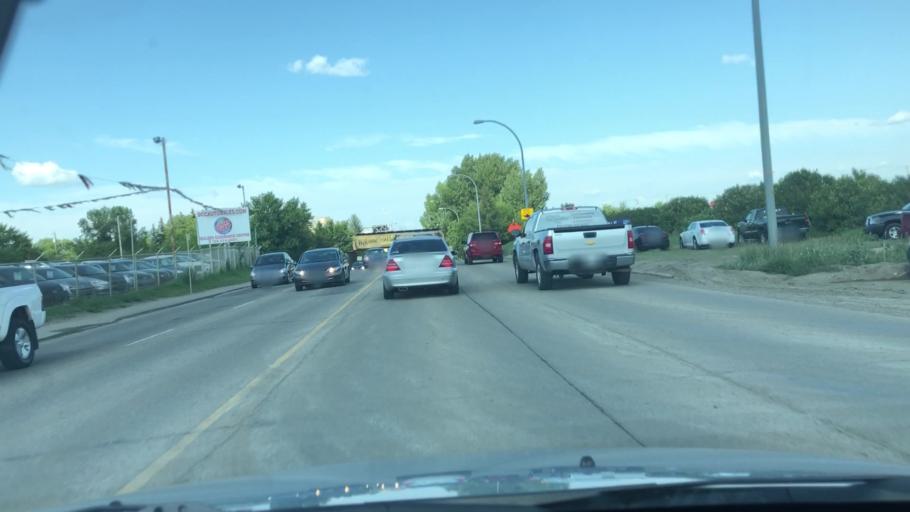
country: CA
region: Alberta
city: Edmonton
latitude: 53.5826
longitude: -113.4484
